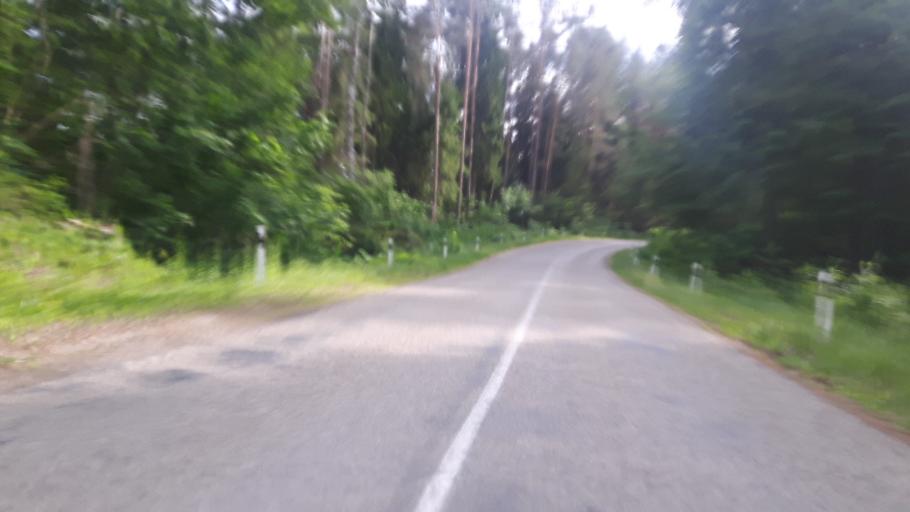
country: LV
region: Engure
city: Smarde
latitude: 56.9928
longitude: 23.3134
